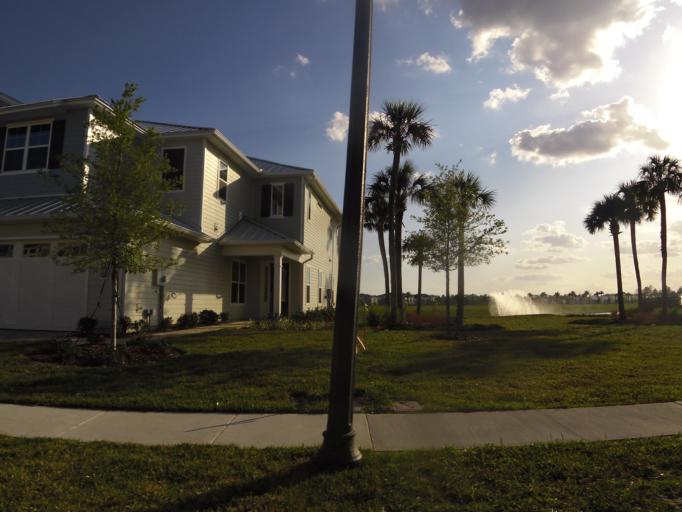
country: US
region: Florida
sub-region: Saint Johns County
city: Palm Valley
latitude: 30.0810
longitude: -81.4842
